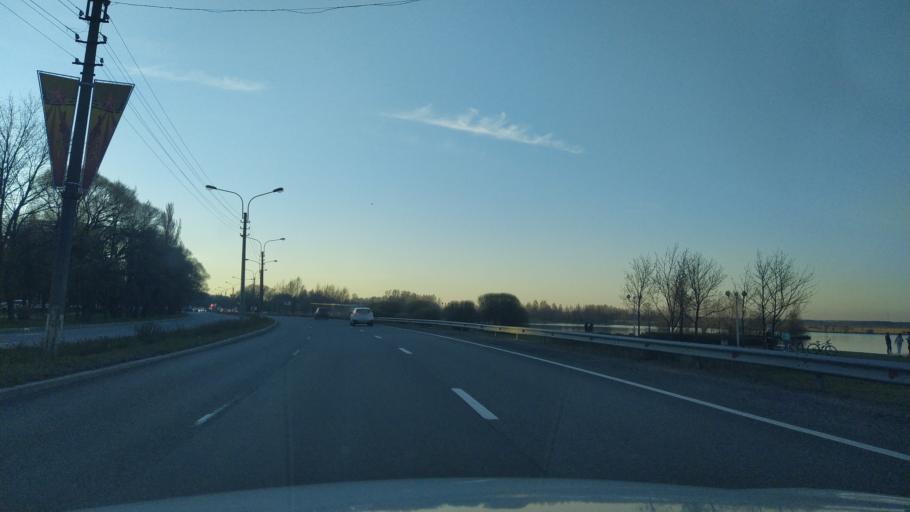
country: RU
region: St.-Petersburg
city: Sestroretsk
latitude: 60.1010
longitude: 29.9799
